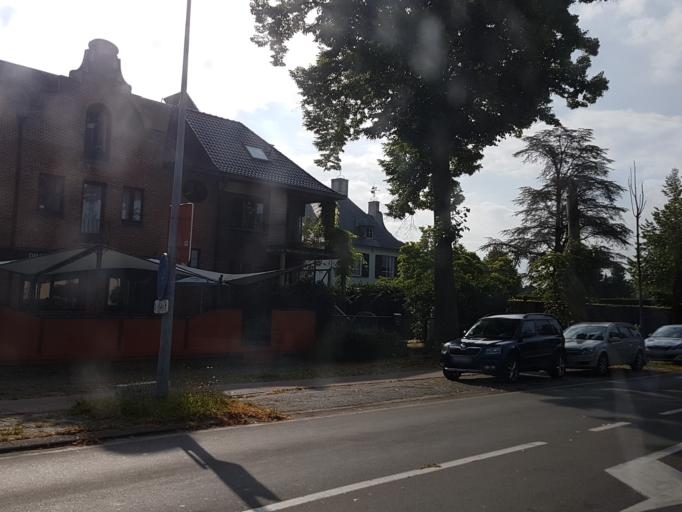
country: BE
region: Flanders
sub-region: Provincie Antwerpen
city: Westerlo
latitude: 51.0898
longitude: 4.9144
